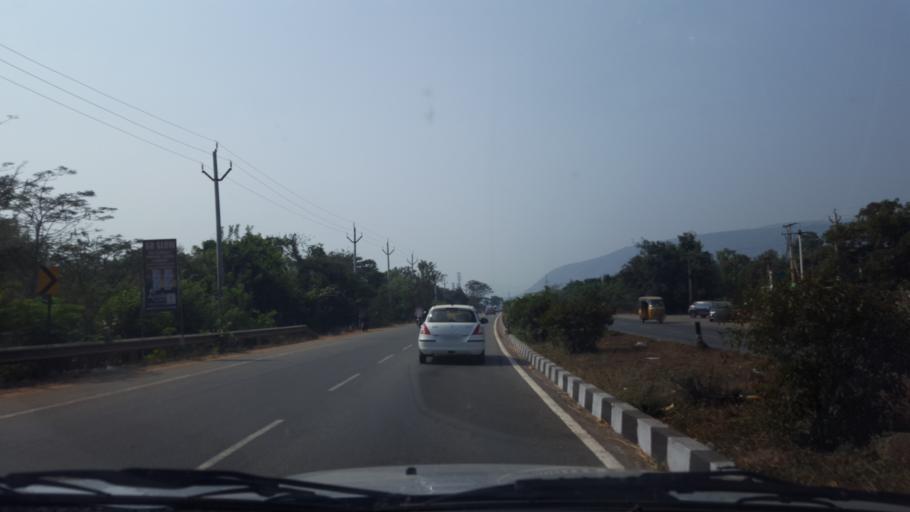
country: IN
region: Andhra Pradesh
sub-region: Vishakhapatnam
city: Bhimunipatnam
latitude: 17.8852
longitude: 83.3777
